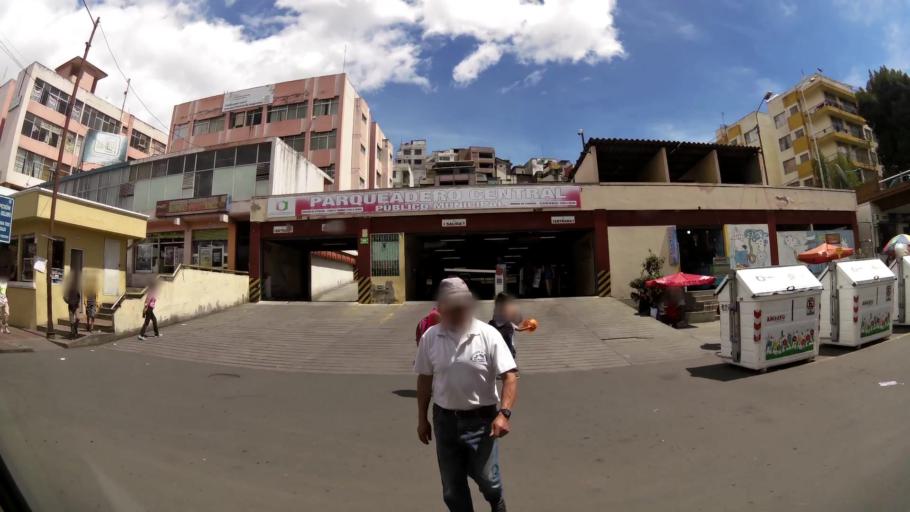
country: EC
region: Tungurahua
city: Ambato
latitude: -1.2431
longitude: -78.6256
